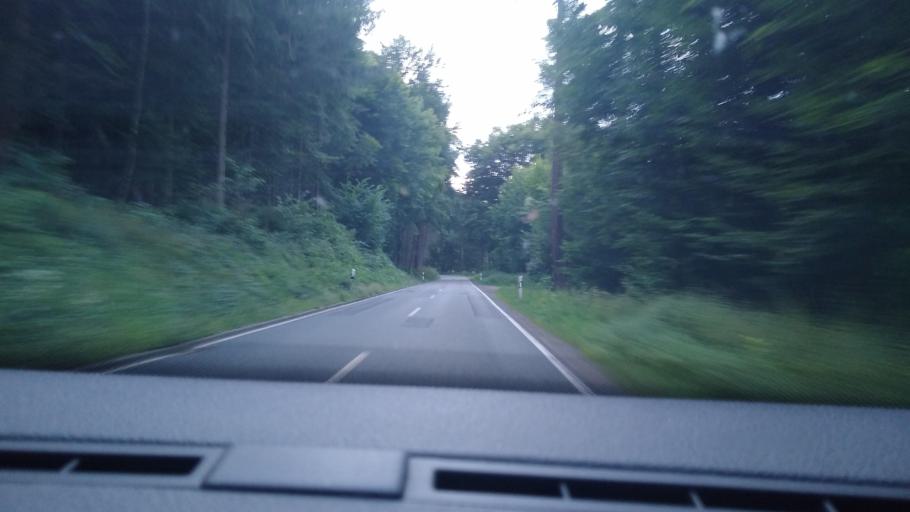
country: DE
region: Hesse
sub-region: Regierungsbezirk Darmstadt
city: Erbach
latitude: 49.6610
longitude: 8.9655
